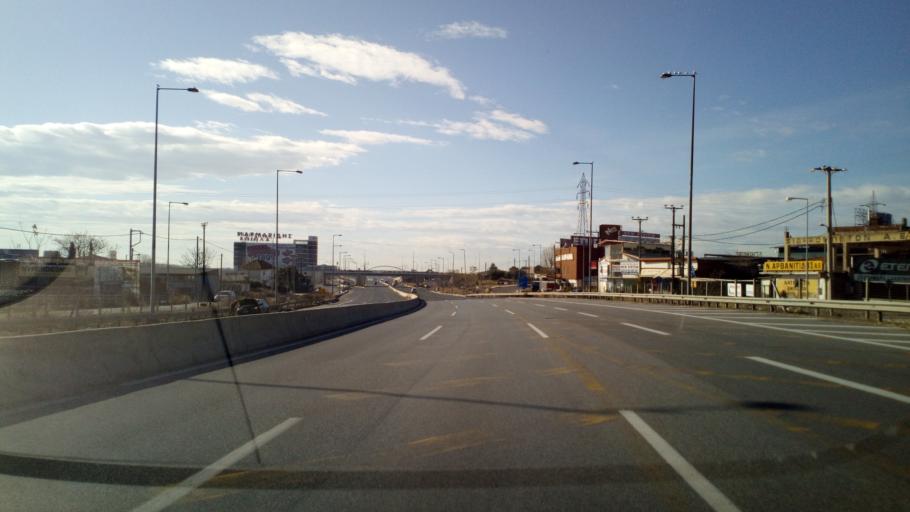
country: GR
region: Central Macedonia
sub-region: Nomos Thessalonikis
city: Efkarpia
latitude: 40.6913
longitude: 22.9447
